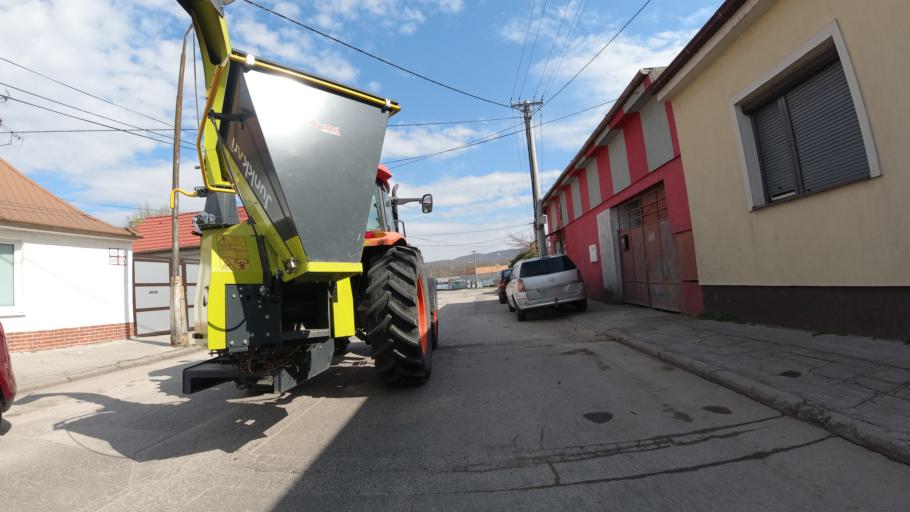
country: SK
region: Trnavsky
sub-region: Okres Trnava
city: Piestany
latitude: 48.6041
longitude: 17.8368
